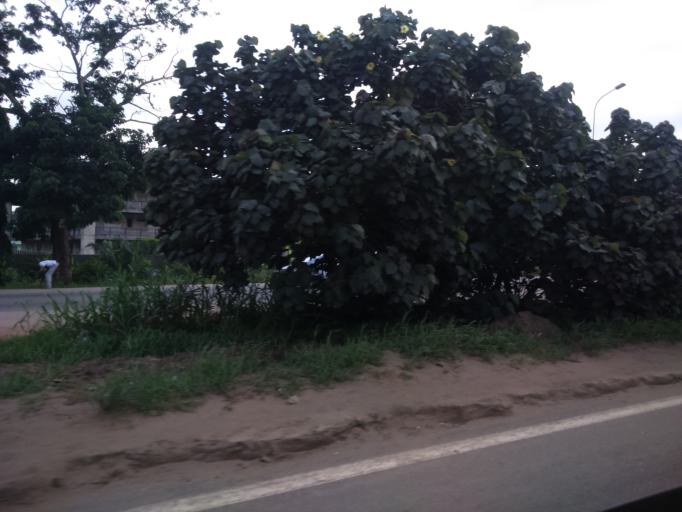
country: CI
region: Lagunes
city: Abobo
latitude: 5.3616
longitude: -4.0844
